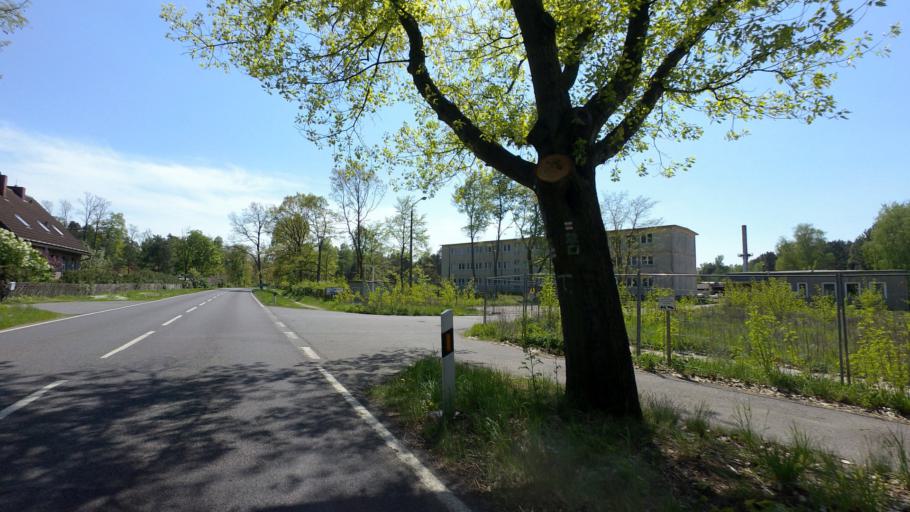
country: DE
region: Brandenburg
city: Gross Koris
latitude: 52.1846
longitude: 13.7055
